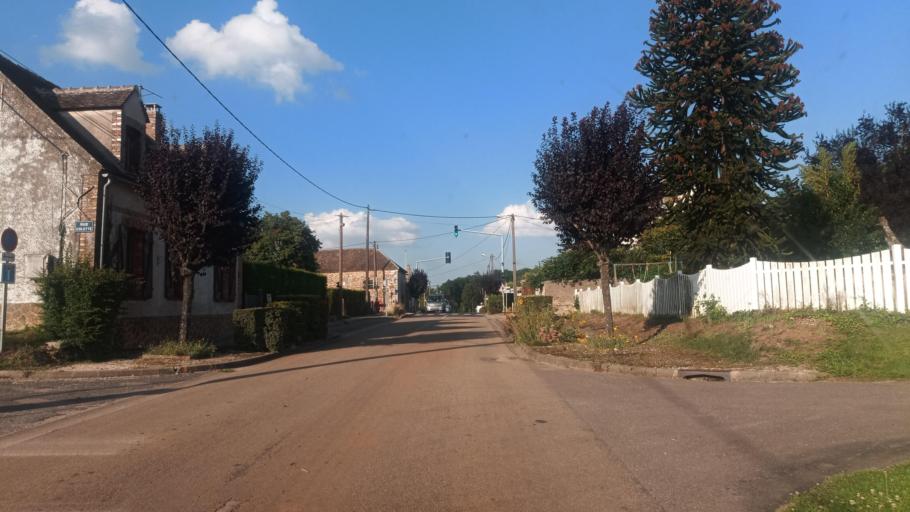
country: FR
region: Bourgogne
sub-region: Departement de l'Yonne
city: Pont-sur-Yonne
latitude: 48.2473
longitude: 3.1568
